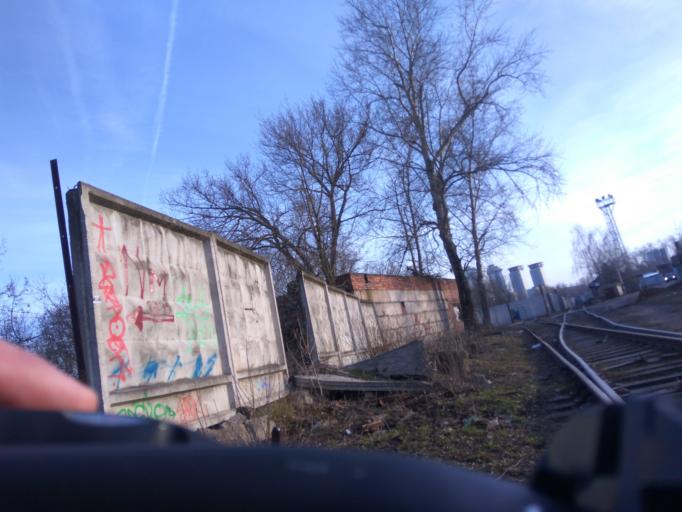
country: RU
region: Moskovskaya
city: Kastanayevo
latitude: 55.7292
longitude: 37.5160
